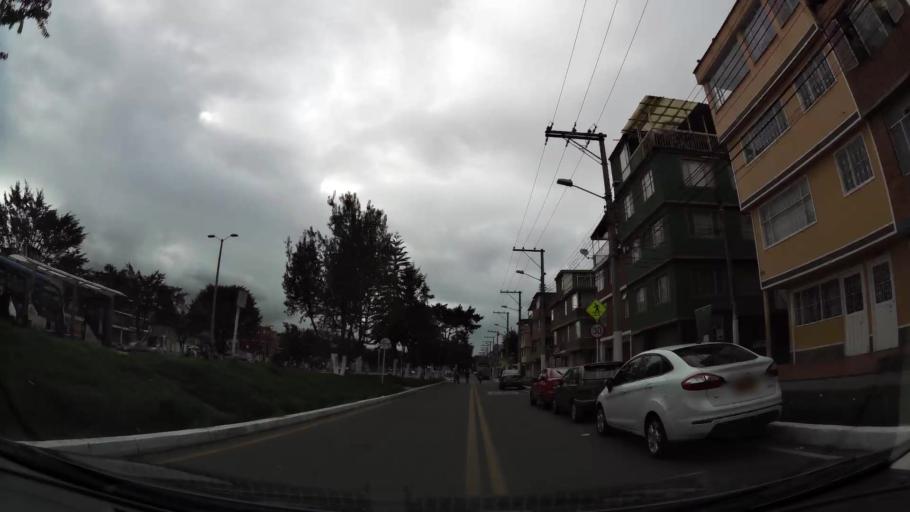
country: CO
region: Bogota D.C.
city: Barrio San Luis
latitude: 4.7151
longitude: -74.0995
